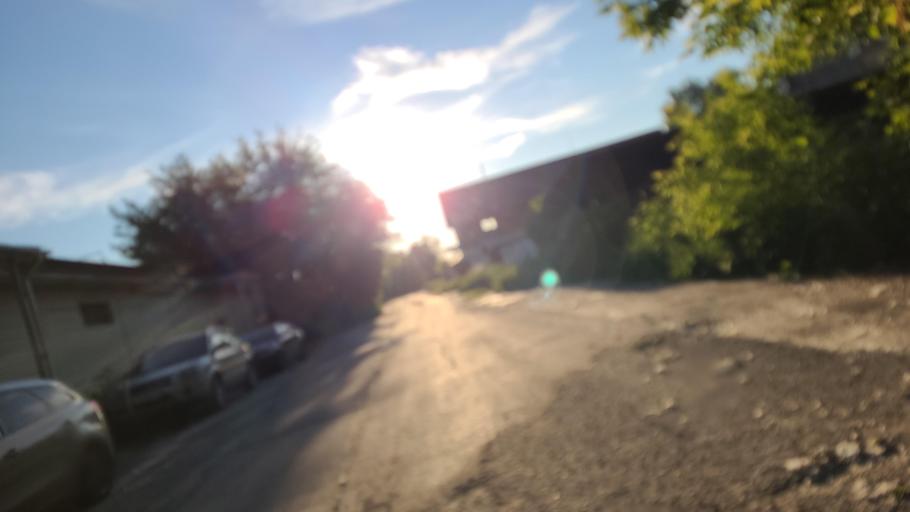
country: RU
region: Moskovskaya
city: Ashitkovo
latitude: 55.4275
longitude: 38.5591
